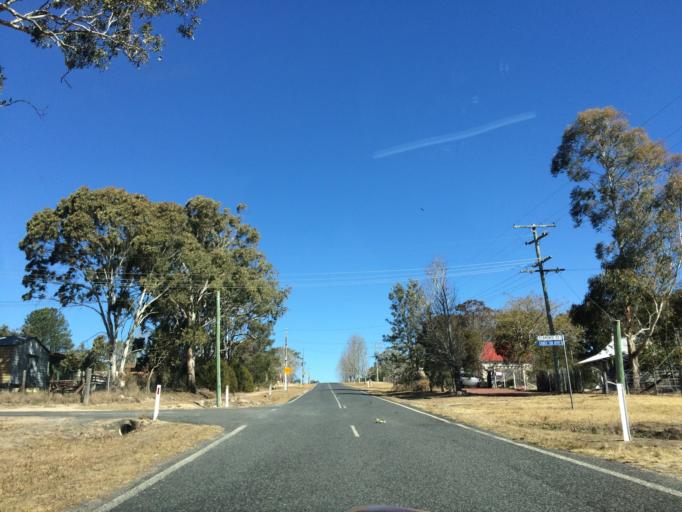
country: AU
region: Queensland
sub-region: Southern Downs
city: Stanthorpe
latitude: -28.6442
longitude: 152.0852
